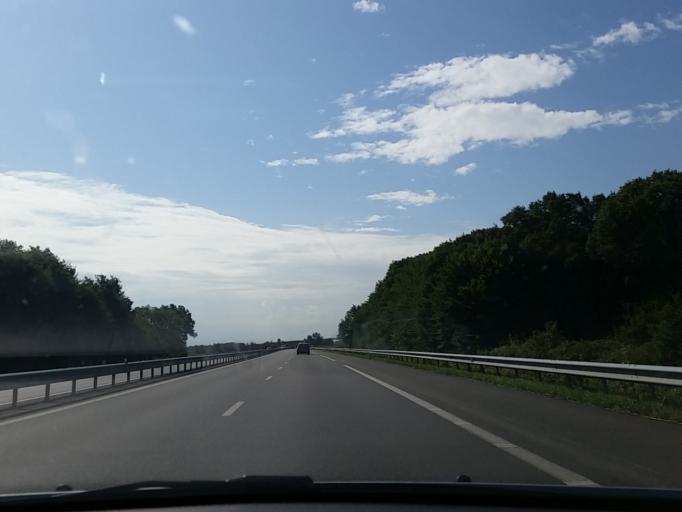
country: FR
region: Centre
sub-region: Departement du Cher
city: Levet
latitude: 46.9369
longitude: 2.4208
